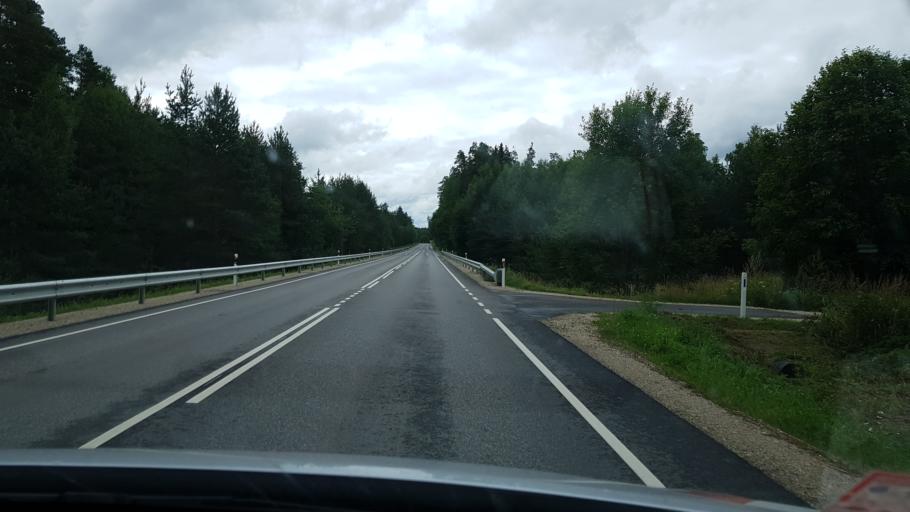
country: EE
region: Polvamaa
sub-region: Polva linn
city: Polva
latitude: 58.0214
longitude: 27.1647
